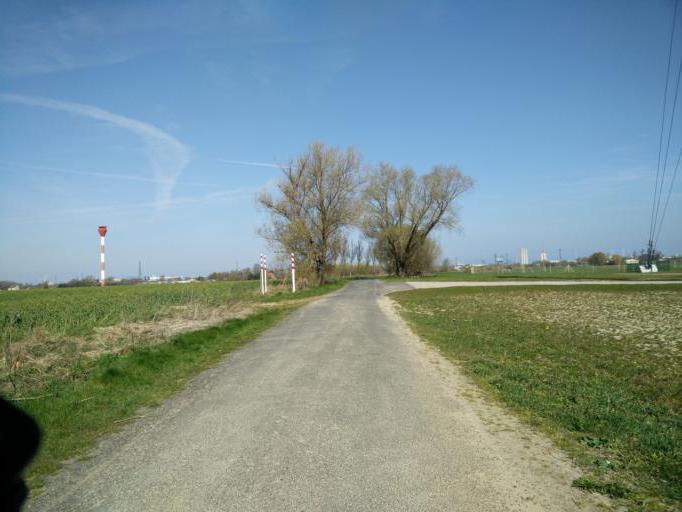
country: DE
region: Mecklenburg-Vorpommern
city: Dierkow-West
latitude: 54.1293
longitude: 12.1262
